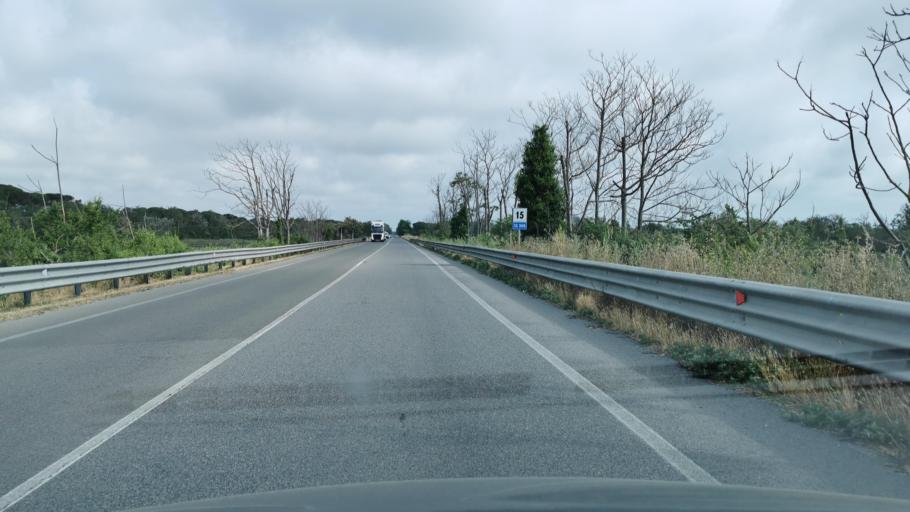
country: IT
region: Emilia-Romagna
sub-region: Provincia di Ravenna
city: Marina Romea
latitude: 44.5850
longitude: 12.2535
